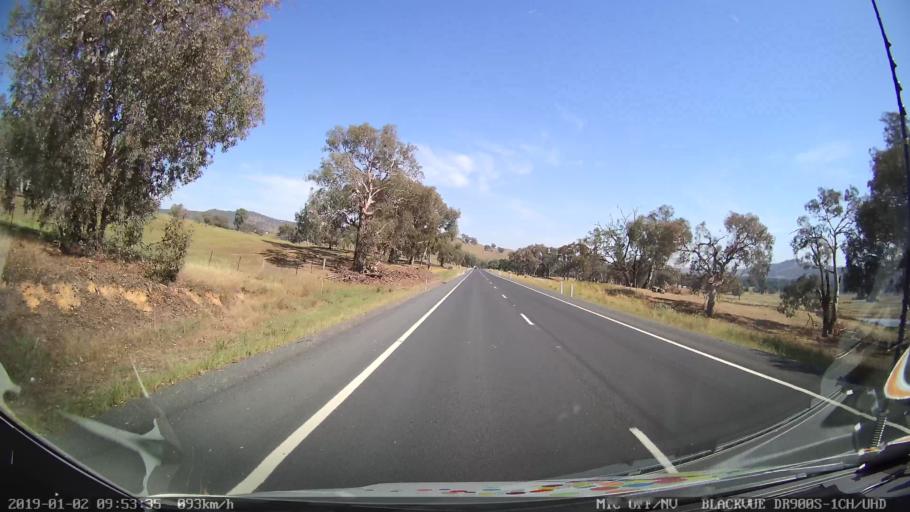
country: AU
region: New South Wales
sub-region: Tumut Shire
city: Tumut
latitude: -35.2461
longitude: 148.2017
